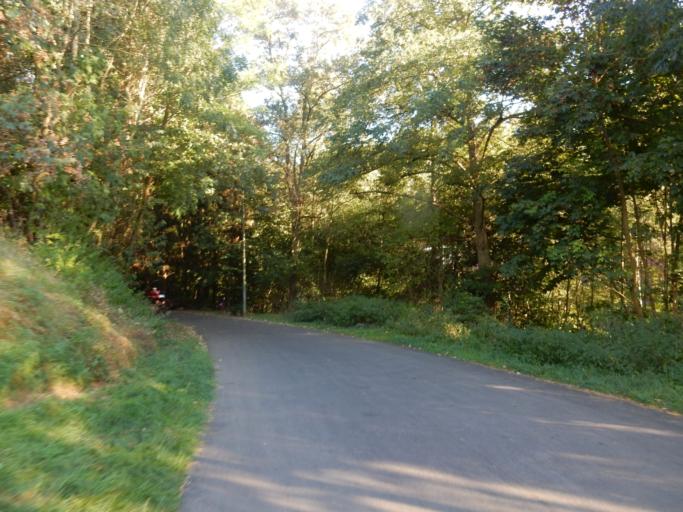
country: LU
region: Luxembourg
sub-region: Canton de Luxembourg
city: Luxembourg
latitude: 49.6011
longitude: 6.1460
